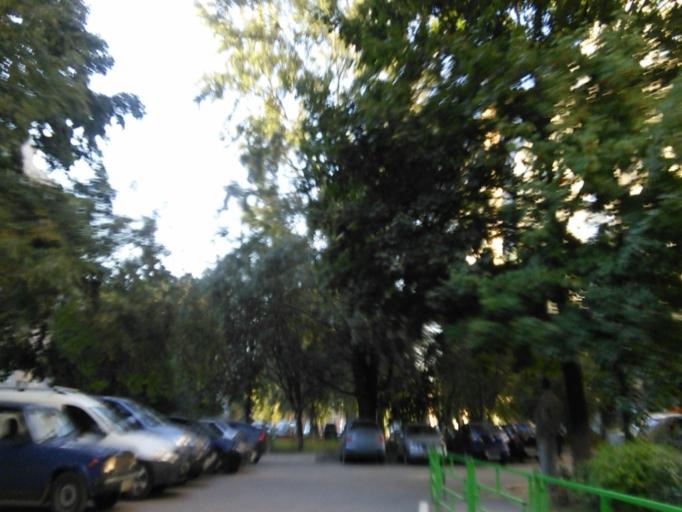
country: RU
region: Moskovskaya
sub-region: Podol'skiy Rayon
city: Podol'sk
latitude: 55.4429
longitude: 37.5651
